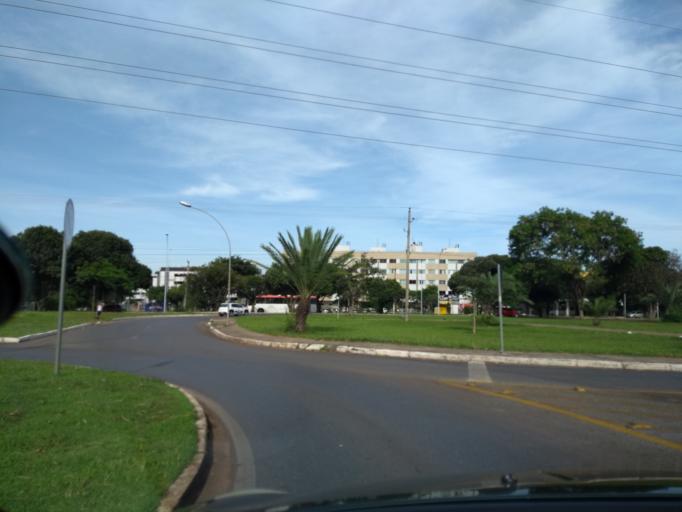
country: BR
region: Federal District
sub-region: Brasilia
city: Brasilia
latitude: -15.7965
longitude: -47.9327
